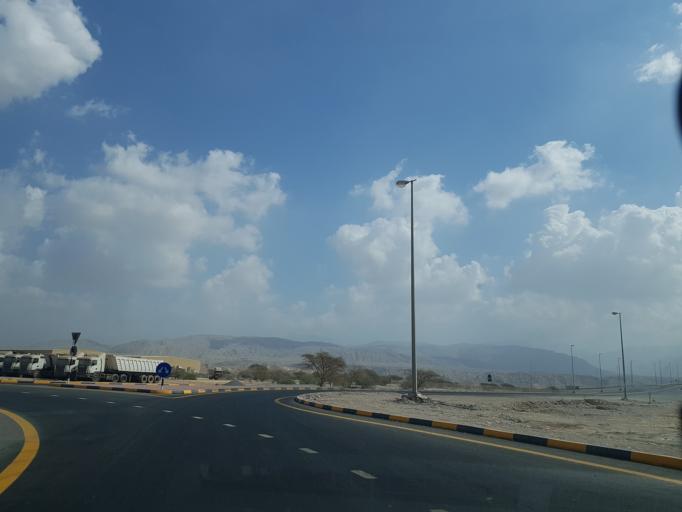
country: AE
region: Ra's al Khaymah
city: Ras al-Khaimah
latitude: 25.7181
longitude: 56.0020
